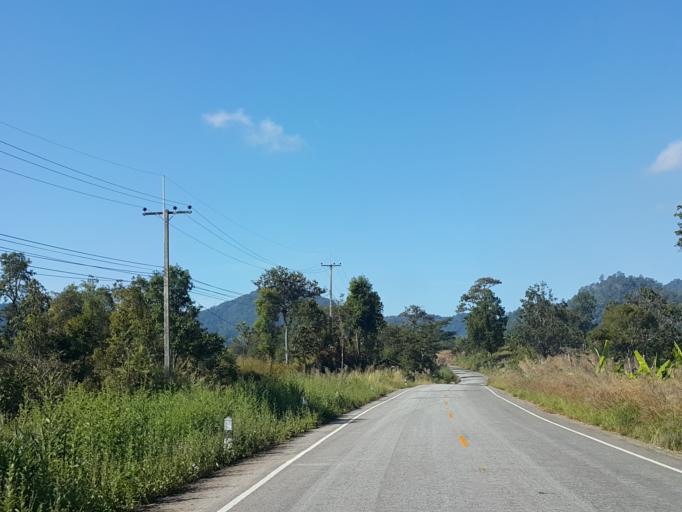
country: TH
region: Chiang Mai
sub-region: Amphoe Chiang Dao
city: Chiang Dao
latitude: 19.5273
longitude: 98.8731
